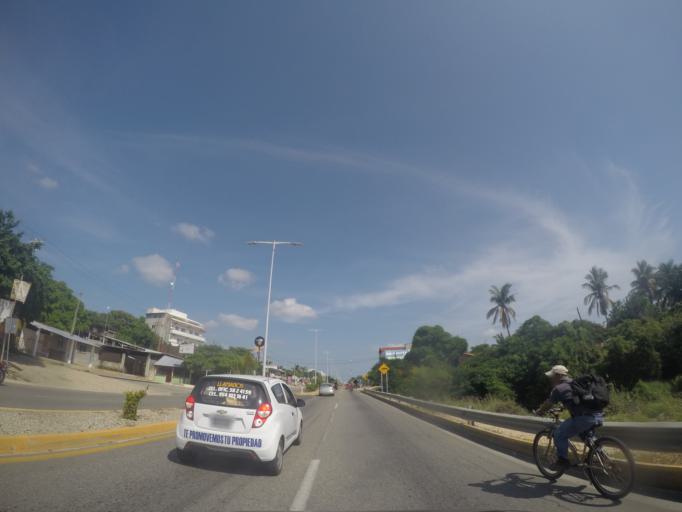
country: MX
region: Oaxaca
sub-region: Santa Maria Colotepec
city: Brisas de Zicatela
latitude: 15.8530
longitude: -97.0530
